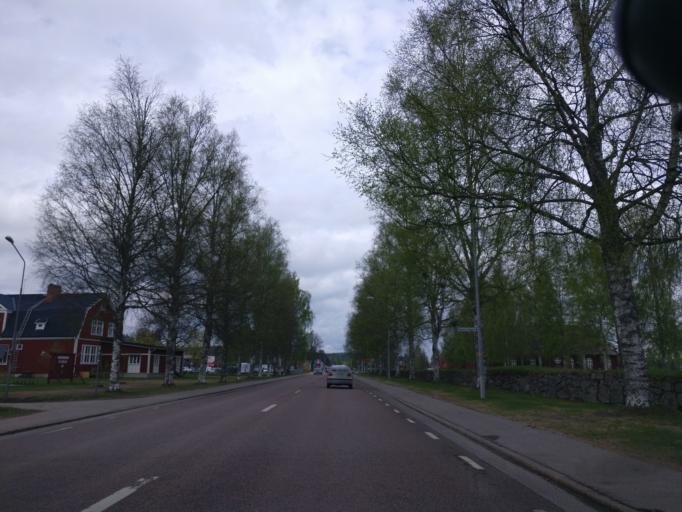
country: SE
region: Vaermland
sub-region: Hagfors Kommun
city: Ekshaerad
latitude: 60.1709
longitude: 13.4971
